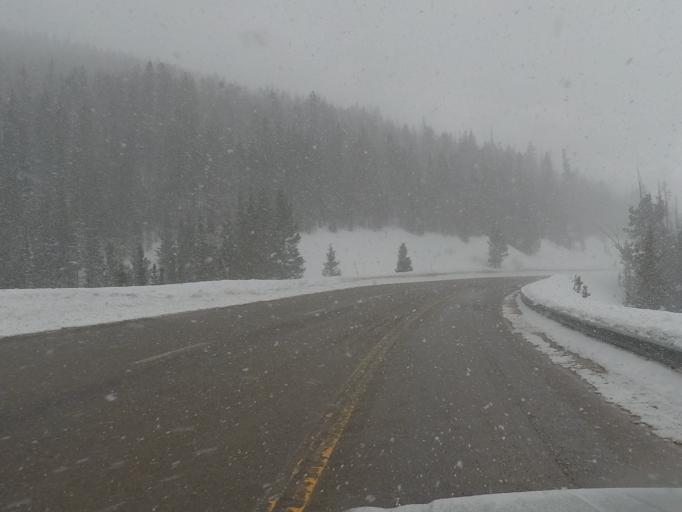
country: US
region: Montana
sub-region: Meagher County
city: White Sulphur Springs
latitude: 46.8335
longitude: -110.6947
